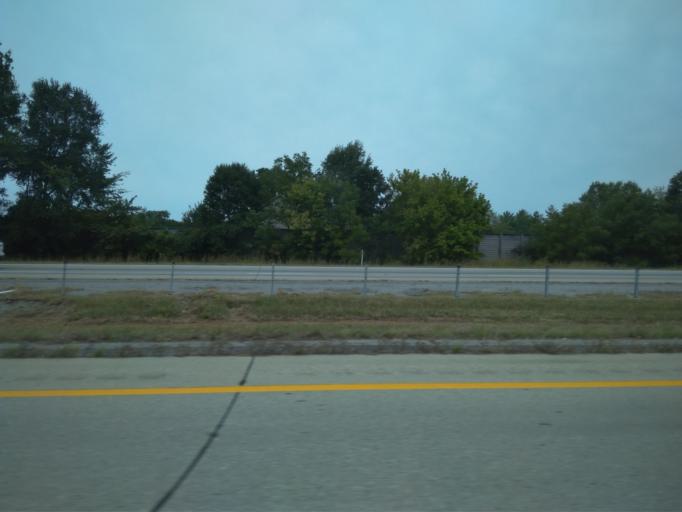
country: US
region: Kentucky
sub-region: Jefferson County
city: Worthington
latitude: 38.3031
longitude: -85.5578
